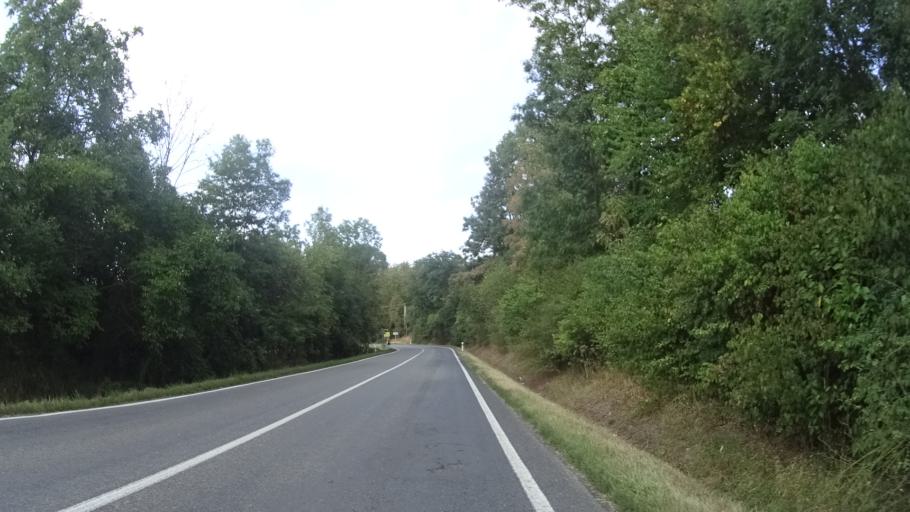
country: CZ
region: Olomoucky
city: Lestina
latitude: 49.8553
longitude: 16.9440
